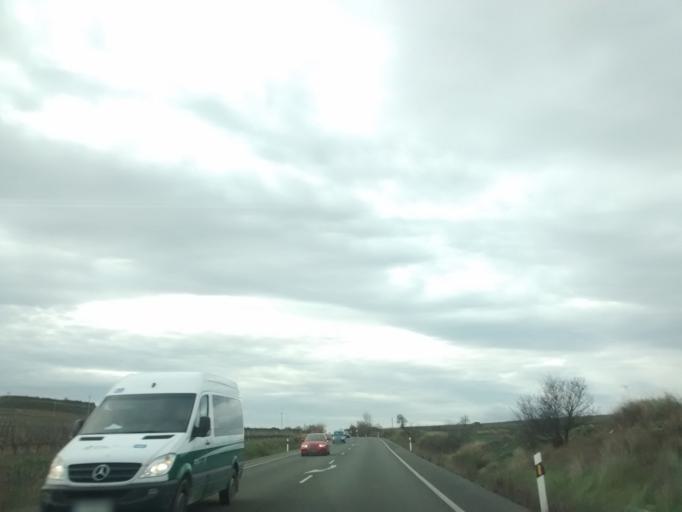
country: ES
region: La Rioja
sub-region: Provincia de La Rioja
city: Briones
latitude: 42.5480
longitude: -2.8023
